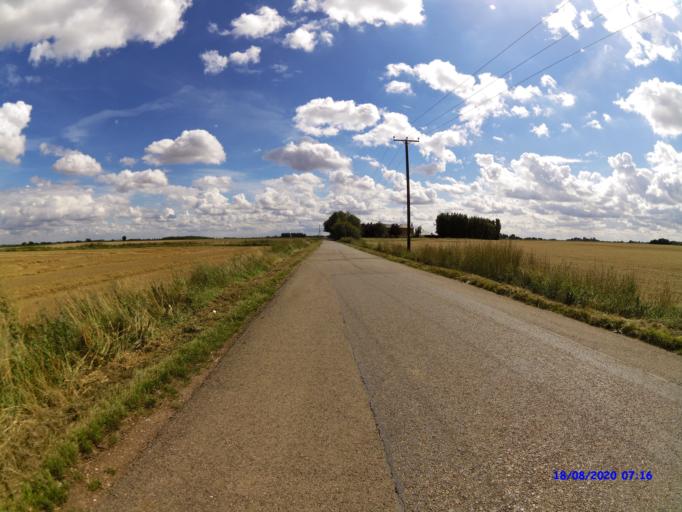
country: GB
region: England
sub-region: Cambridgeshire
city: Whittlesey
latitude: 52.5359
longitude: -0.1062
